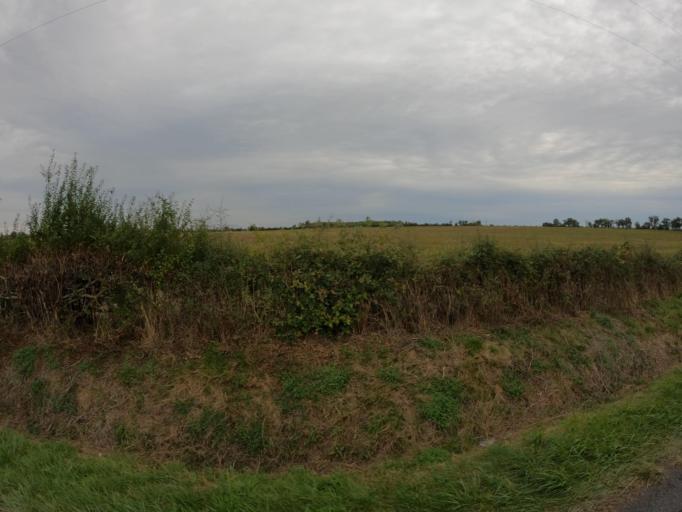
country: FR
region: Poitou-Charentes
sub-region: Departement de la Vienne
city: Saulge
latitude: 46.3705
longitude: 0.8414
